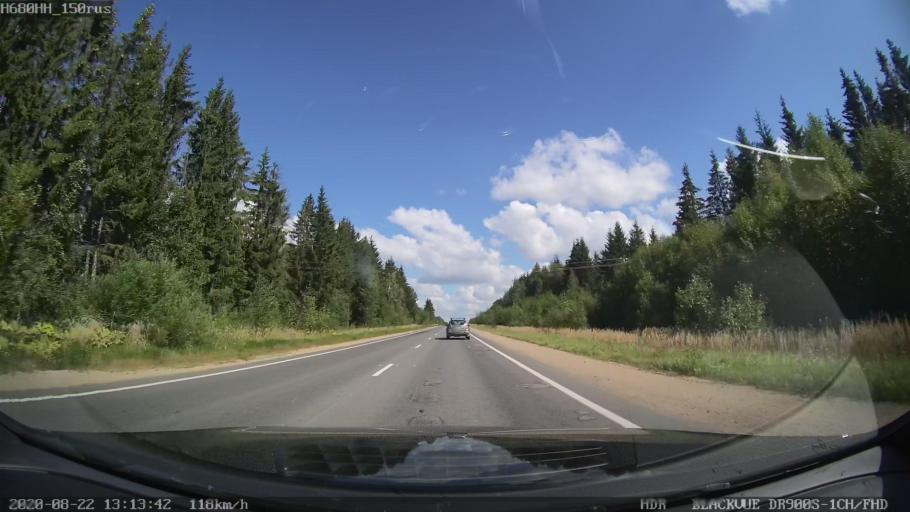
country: RU
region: Tverskaya
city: Bezhetsk
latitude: 57.7519
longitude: 36.5806
